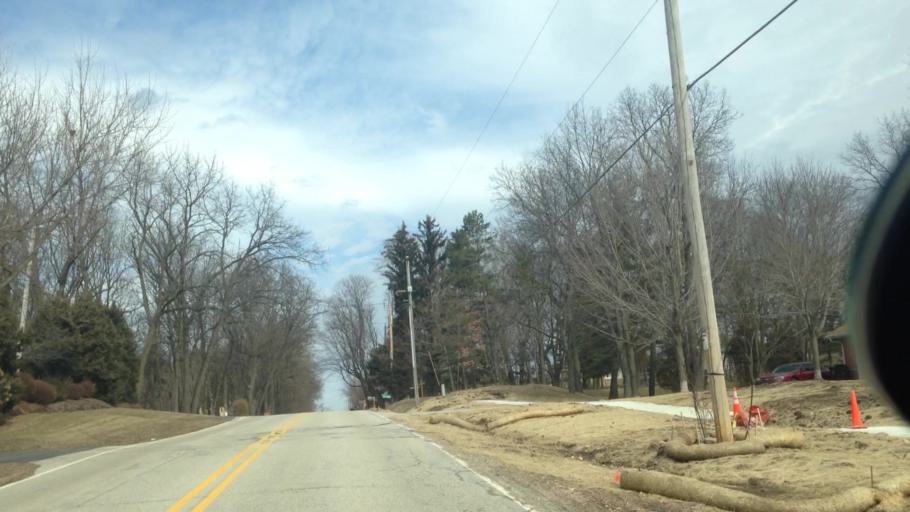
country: US
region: Wisconsin
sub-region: Waukesha County
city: Sussex
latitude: 43.1541
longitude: -88.2236
